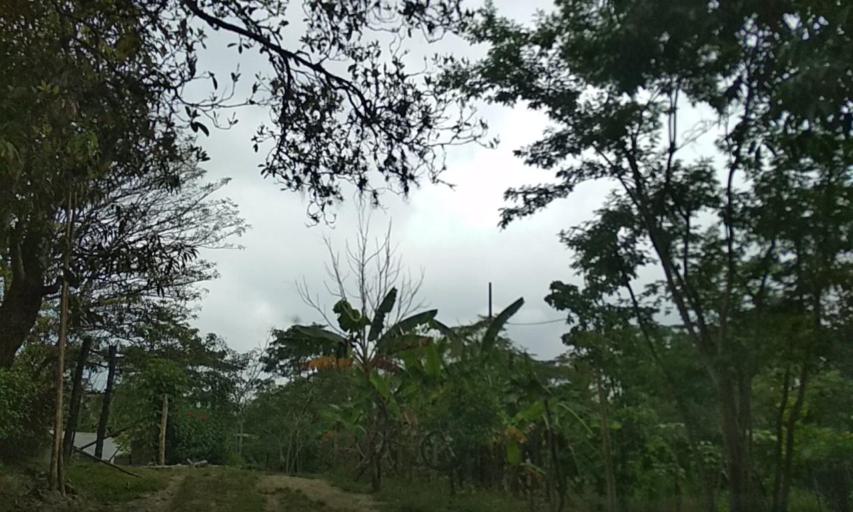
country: MX
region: Tabasco
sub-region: Huimanguillo
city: Francisco Rueda
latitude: 17.6571
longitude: -94.0970
